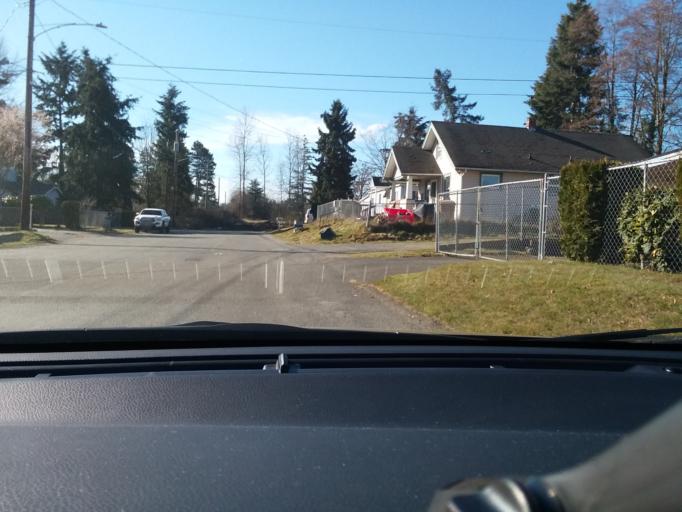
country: US
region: Washington
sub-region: Pierce County
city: Midland
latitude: 47.2060
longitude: -122.4099
